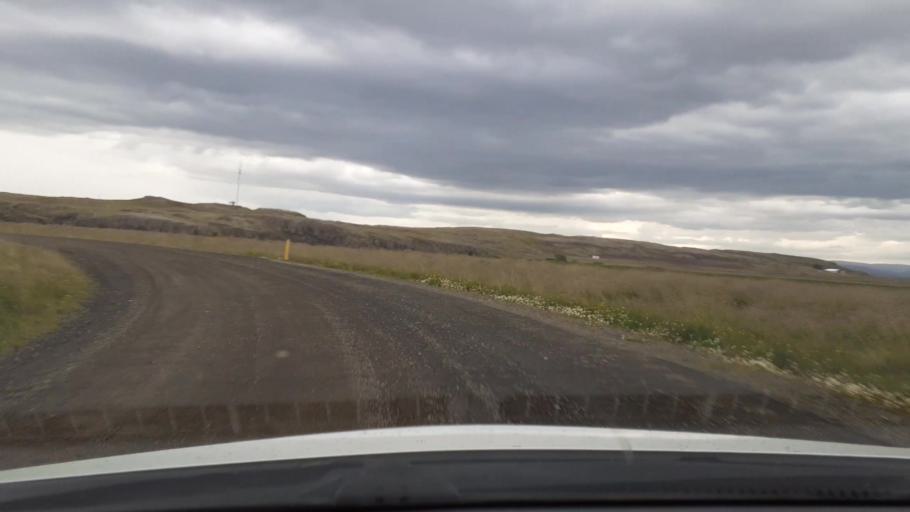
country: IS
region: West
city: Borgarnes
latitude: 64.6030
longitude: -21.6972
